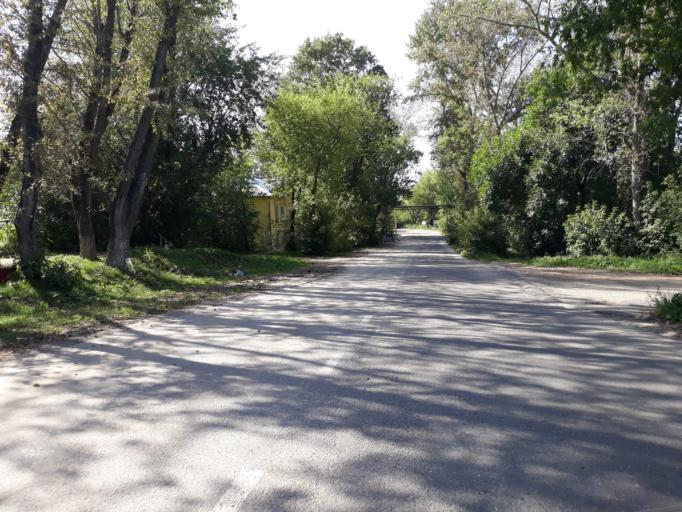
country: RU
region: Jaroslavl
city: Yaroslavl
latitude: 57.5955
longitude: 39.8581
